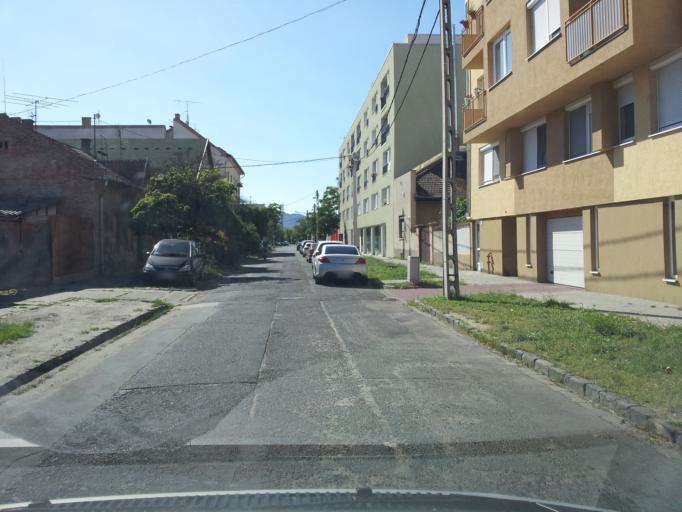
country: HU
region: Budapest
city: Budapest XIII. keruelet
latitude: 47.5353
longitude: 19.0901
